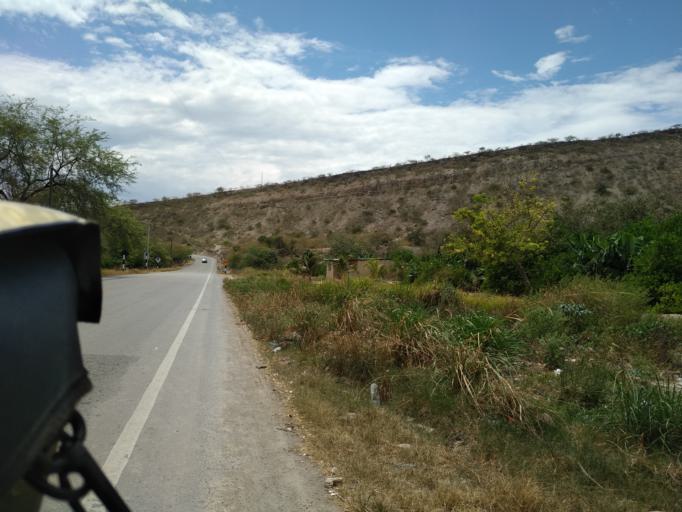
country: PE
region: Cajamarca
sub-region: Provincia de Jaen
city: Bellavista
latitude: -5.7443
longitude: -78.6598
